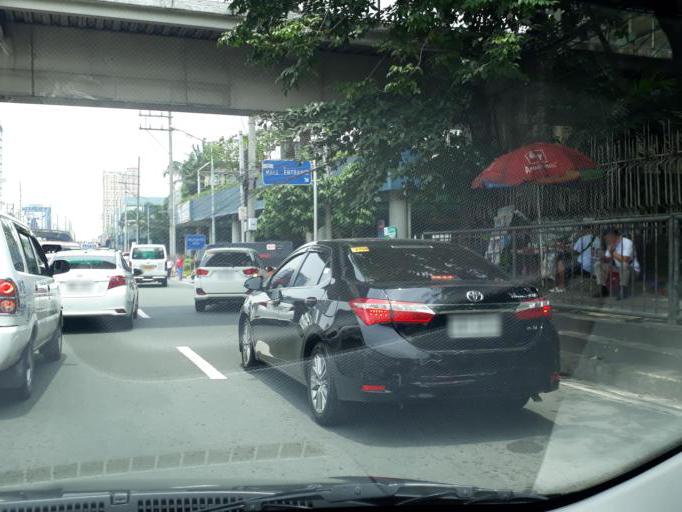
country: PH
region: Calabarzon
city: Bagong Pagasa
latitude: 14.6552
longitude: 121.0323
